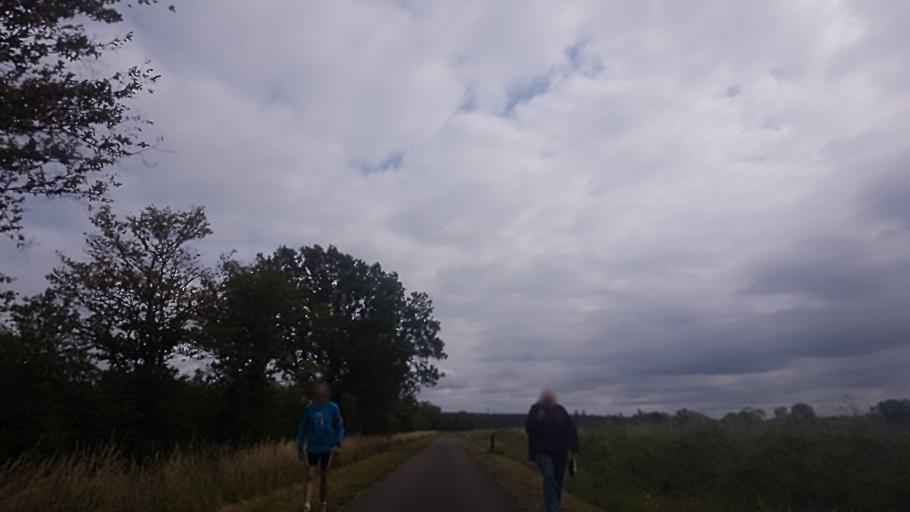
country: BE
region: Wallonia
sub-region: Province de Namur
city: Couvin
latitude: 50.1006
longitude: 4.5434
